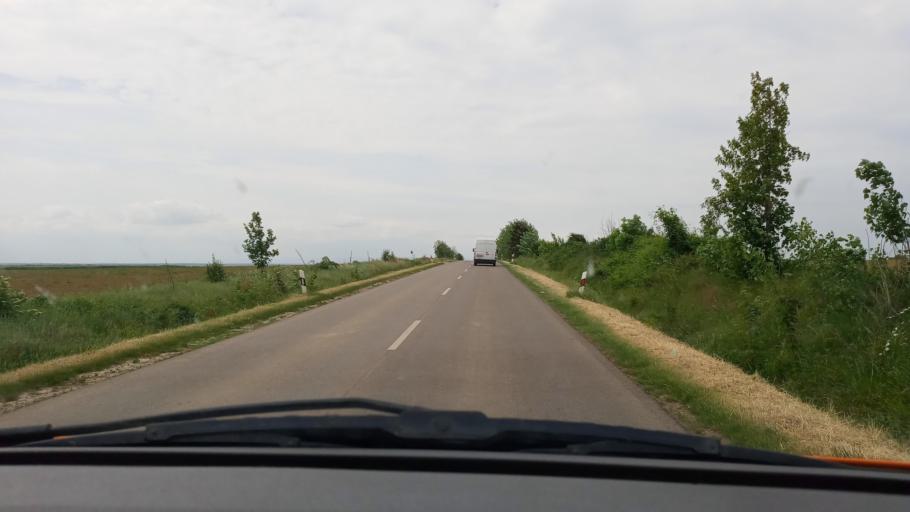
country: HU
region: Baranya
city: Vajszlo
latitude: 45.9385
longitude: 18.0728
